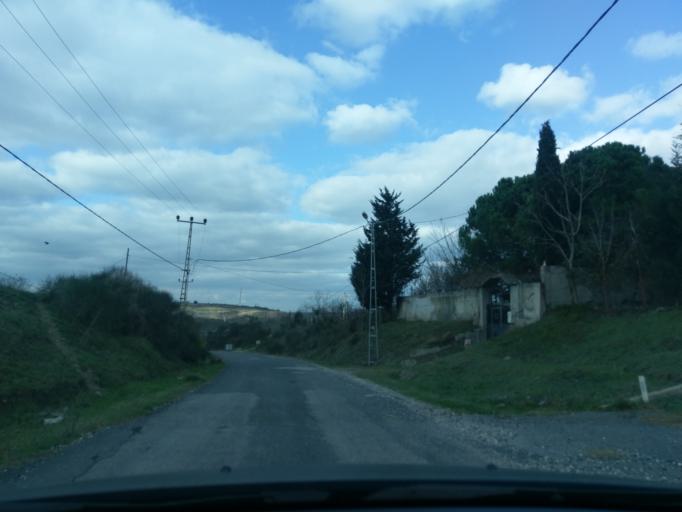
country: TR
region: Istanbul
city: Durusu
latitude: 41.2936
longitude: 28.6815
